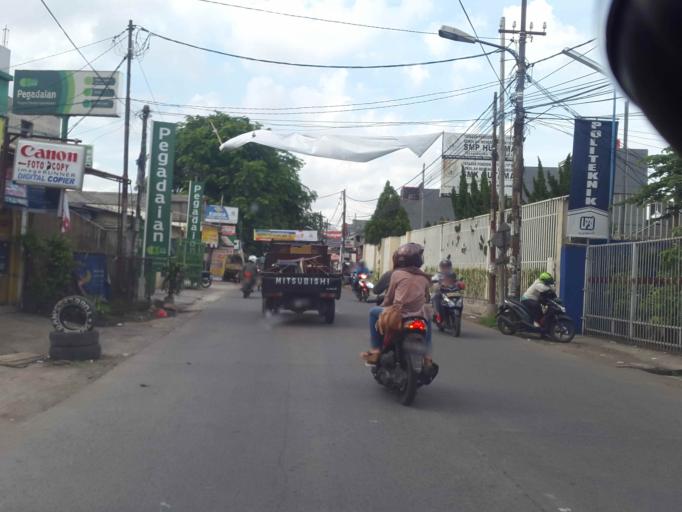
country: ID
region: West Java
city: Bekasi
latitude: -6.2870
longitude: 106.9141
